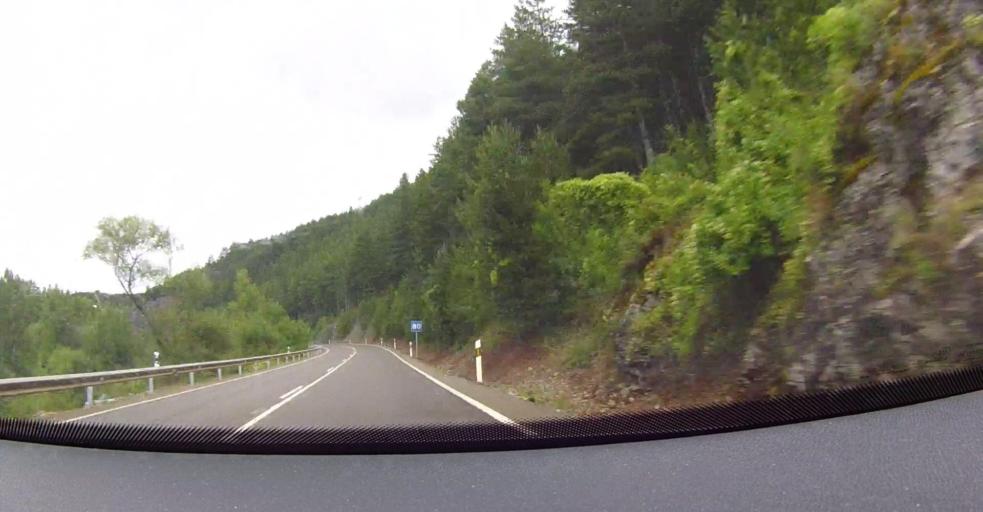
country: ES
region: Castille and Leon
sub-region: Provincia de Leon
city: Cistierna
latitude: 42.8220
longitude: -5.1208
